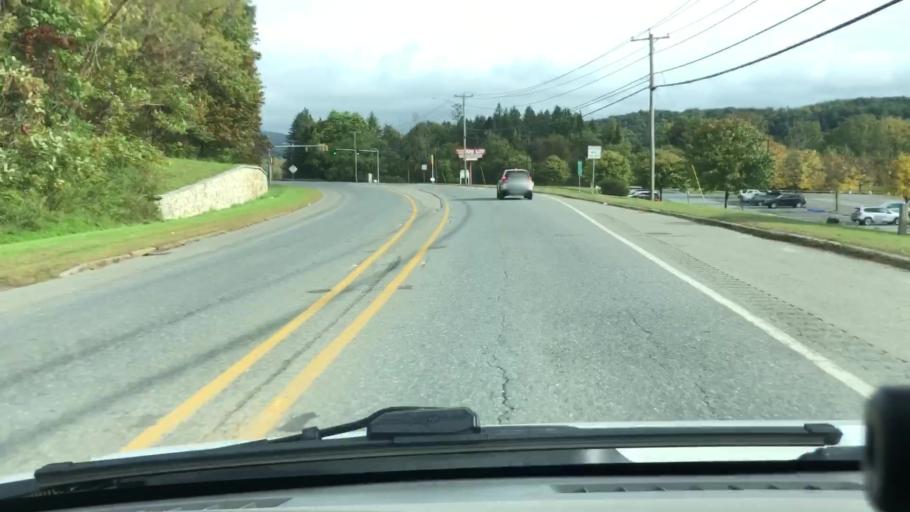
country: US
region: Massachusetts
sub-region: Berkshire County
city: North Adams
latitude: 42.6791
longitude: -73.1066
